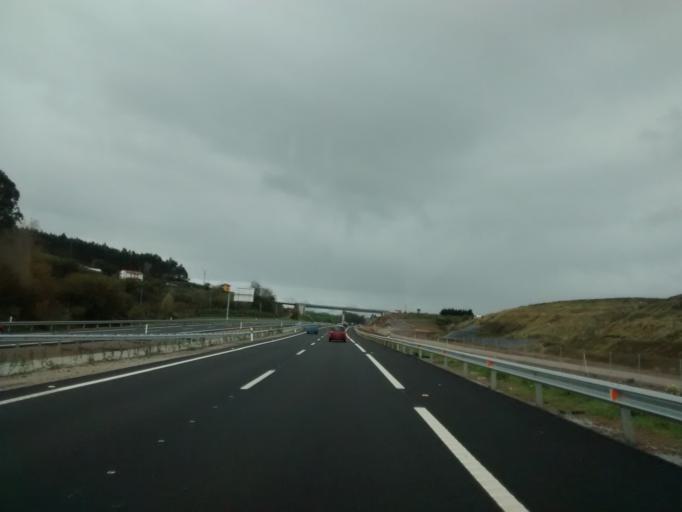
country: ES
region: Cantabria
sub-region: Provincia de Cantabria
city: Polanco
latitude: 43.3459
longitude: -4.0056
